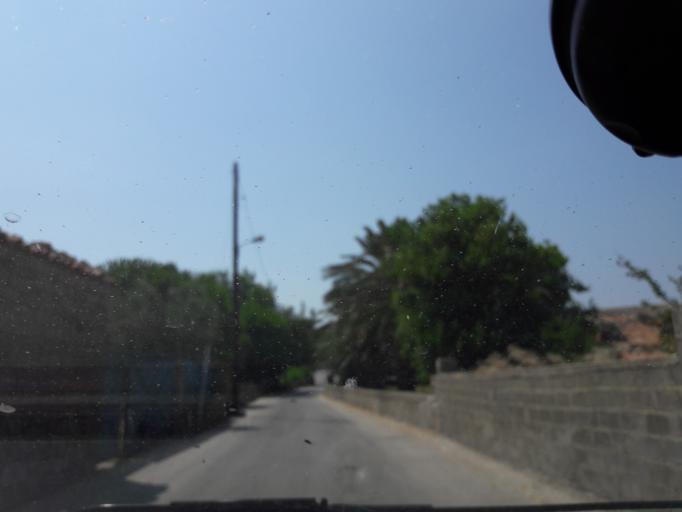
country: GR
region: North Aegean
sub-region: Nomos Lesvou
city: Myrina
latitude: 39.9045
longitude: 25.2894
